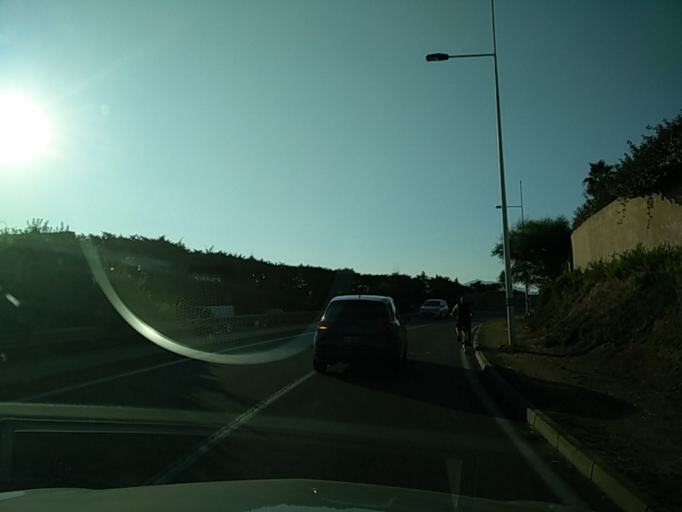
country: FR
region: Corsica
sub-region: Departement de la Corse-du-Sud
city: Pietrosella
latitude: 41.8690
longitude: 8.7877
